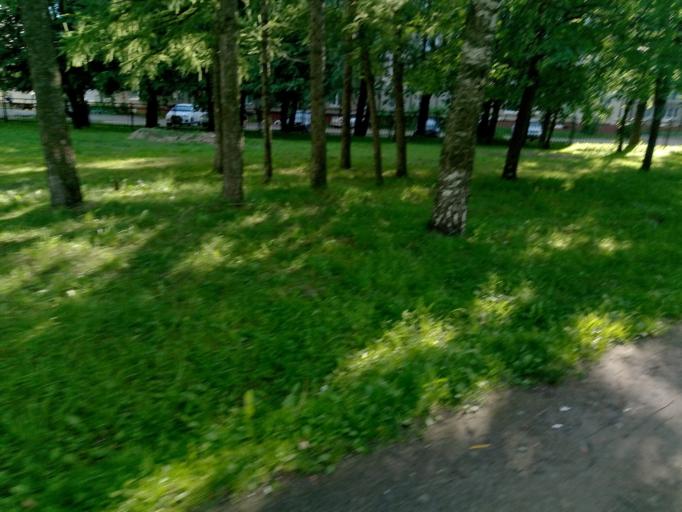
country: RU
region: Jaroslavl
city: Yaroslavl
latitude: 57.6529
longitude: 39.9539
